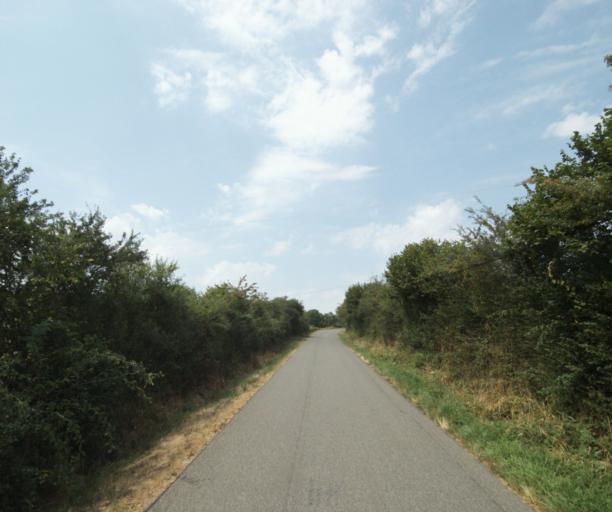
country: FR
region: Bourgogne
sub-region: Departement de Saone-et-Loire
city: Gueugnon
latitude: 46.6050
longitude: 4.0027
